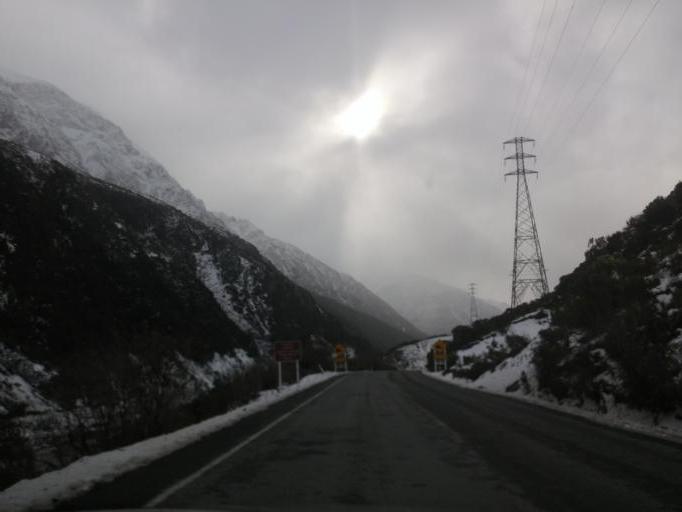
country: NZ
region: West Coast
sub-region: Grey District
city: Greymouth
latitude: -42.8928
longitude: 171.5578
